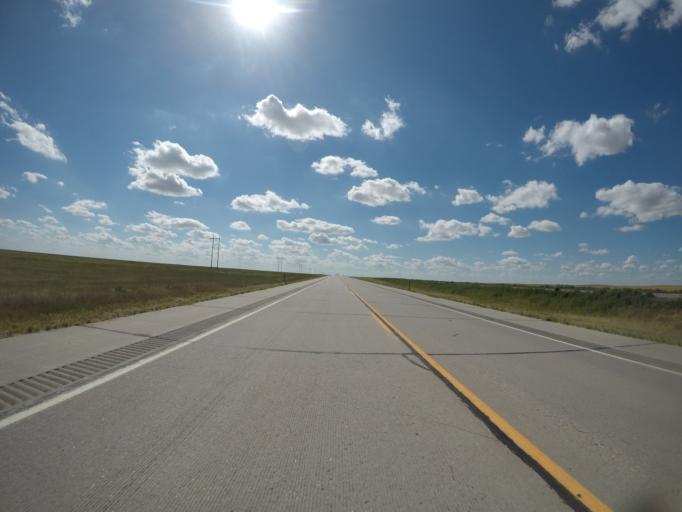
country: US
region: Colorado
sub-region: Phillips County
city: Holyoke
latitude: 40.6006
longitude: -102.4009
